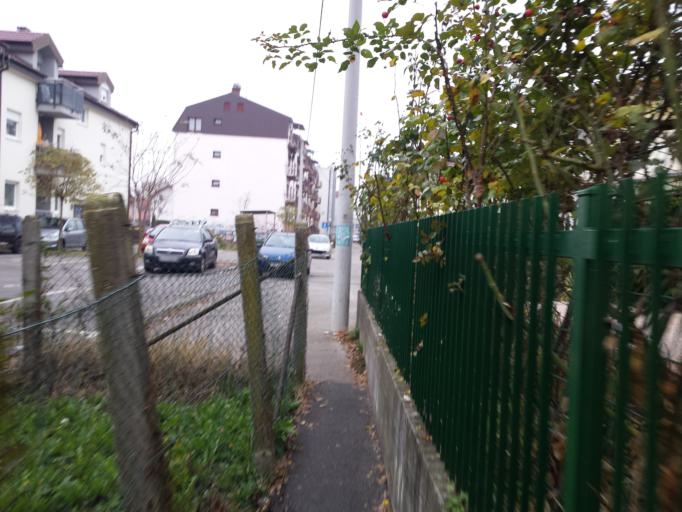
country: HR
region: Grad Zagreb
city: Stenjevec
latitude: 45.8100
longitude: 15.9001
